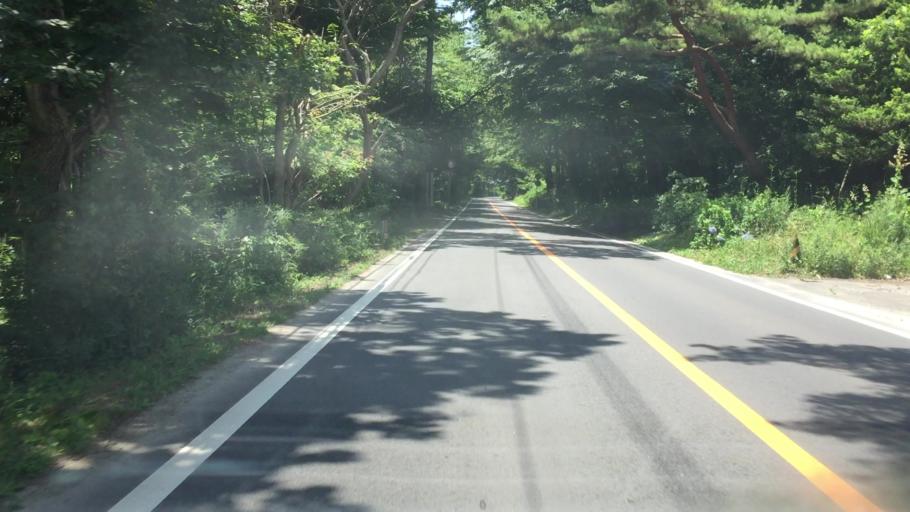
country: JP
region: Tochigi
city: Kuroiso
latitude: 37.0279
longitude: 139.9830
